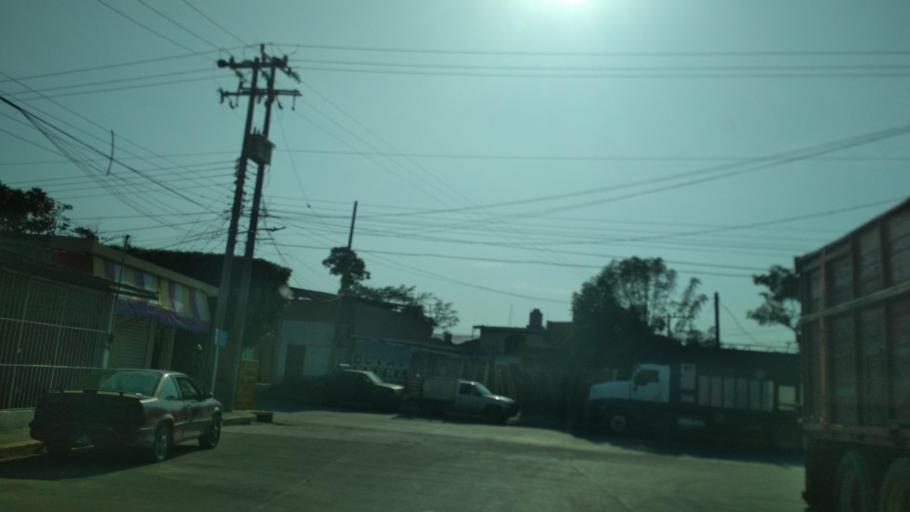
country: MM
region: Shan
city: Taunggyi
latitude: 20.3985
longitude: 97.3352
